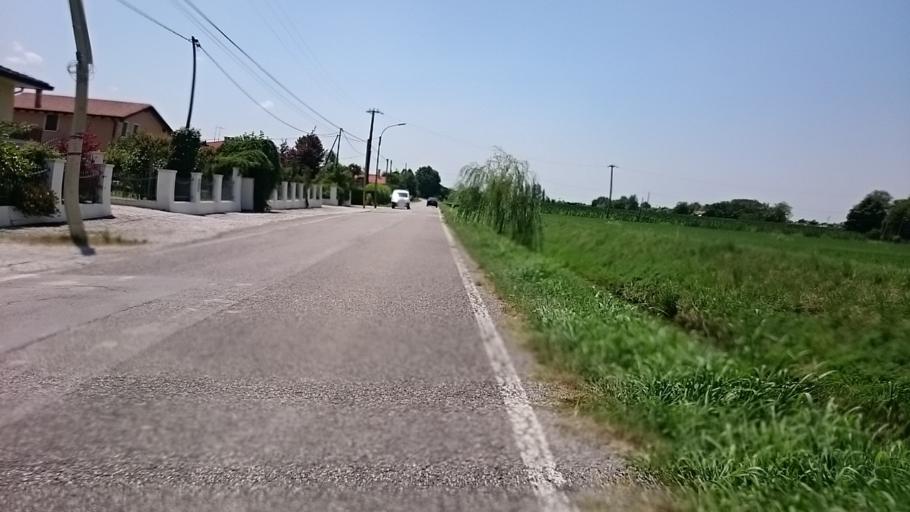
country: IT
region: Veneto
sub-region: Provincia di Venezia
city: Sant'Angelo
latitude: 45.5149
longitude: 11.9962
